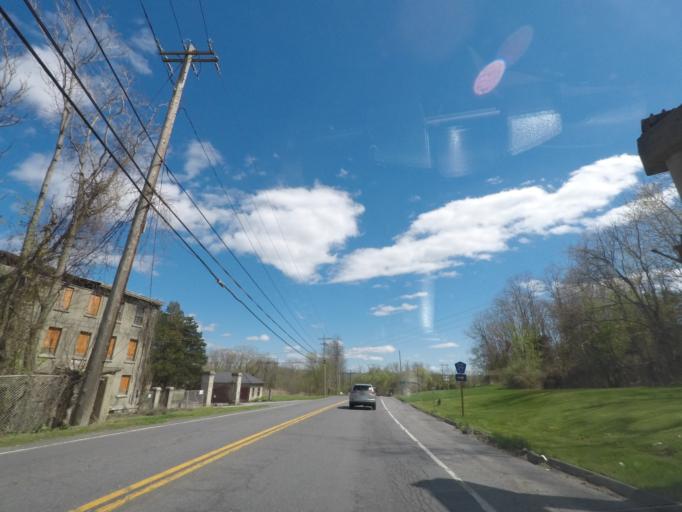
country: US
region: New York
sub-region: Columbia County
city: Oakdale
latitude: 42.2394
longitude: -73.7595
